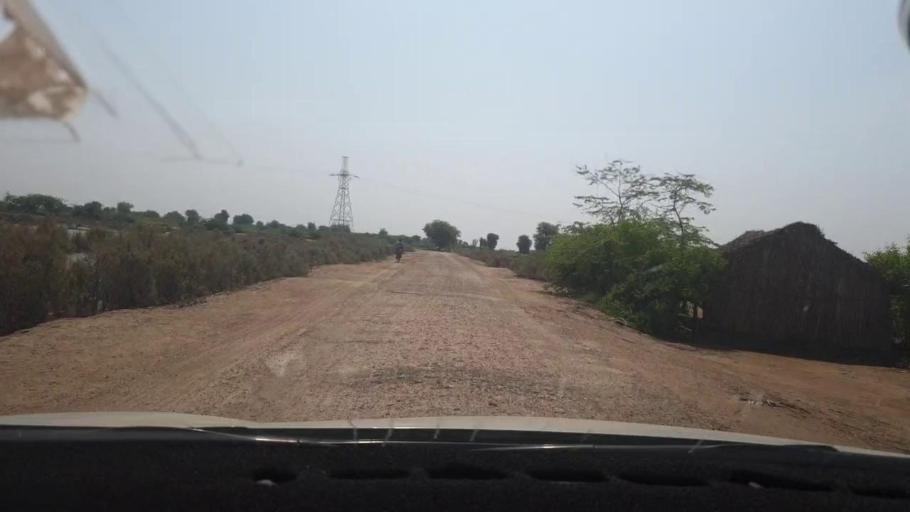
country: PK
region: Sindh
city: Tando Mittha Khan
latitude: 25.9183
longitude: 69.2348
